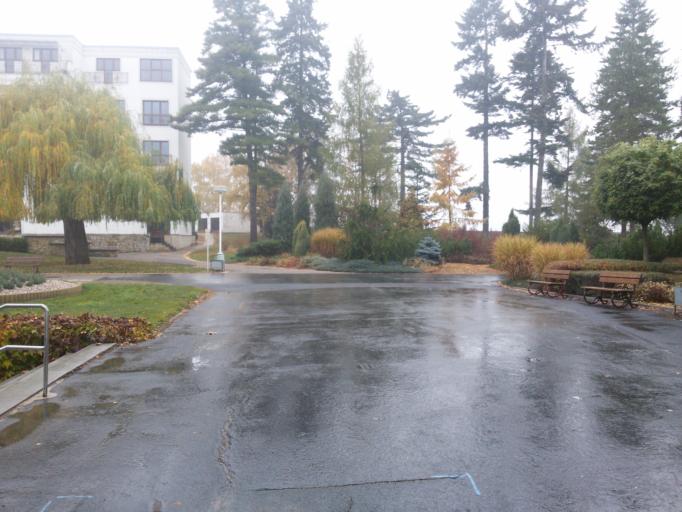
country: CZ
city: Cernozice
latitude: 50.3561
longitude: 15.8481
